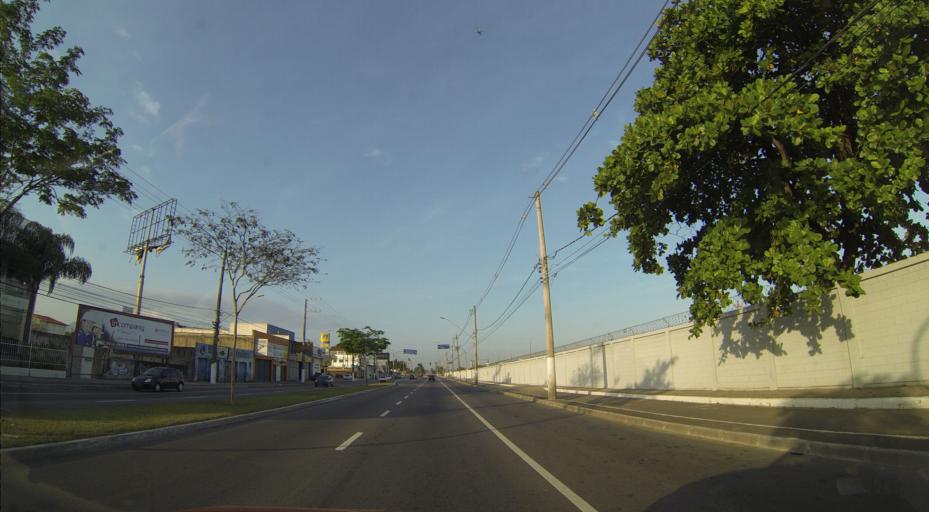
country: BR
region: Espirito Santo
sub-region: Vila Velha
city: Vila Velha
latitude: -20.2602
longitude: -40.2926
